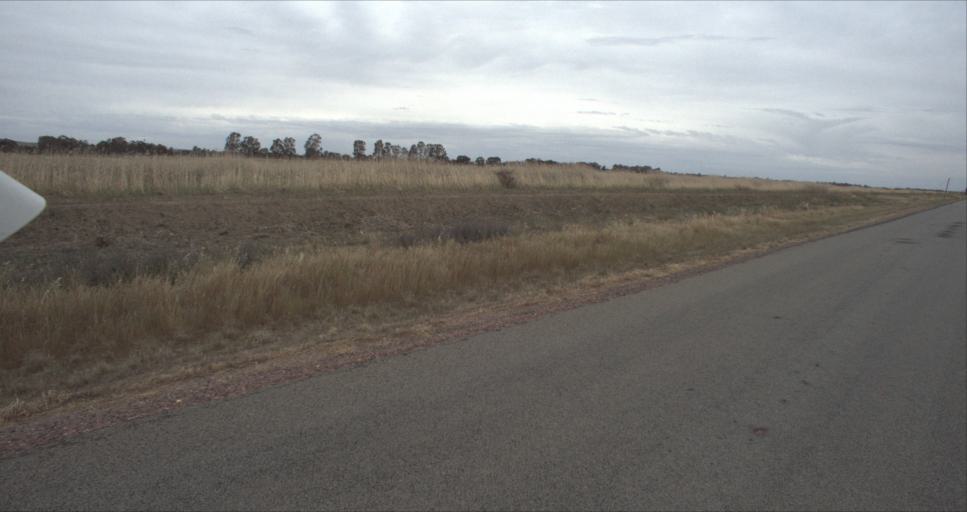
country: AU
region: New South Wales
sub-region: Leeton
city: Leeton
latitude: -34.4883
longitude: 146.4020
